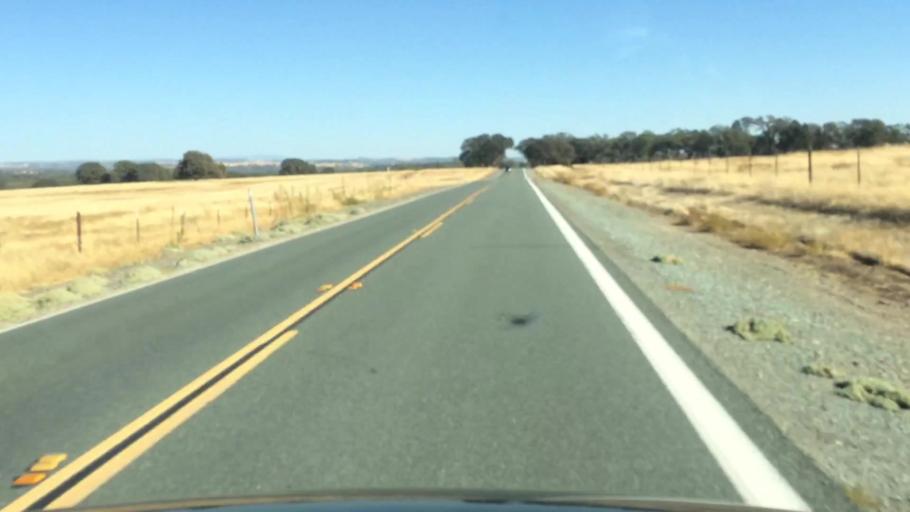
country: US
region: California
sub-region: Amador County
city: Ione
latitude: 38.3854
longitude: -121.0048
